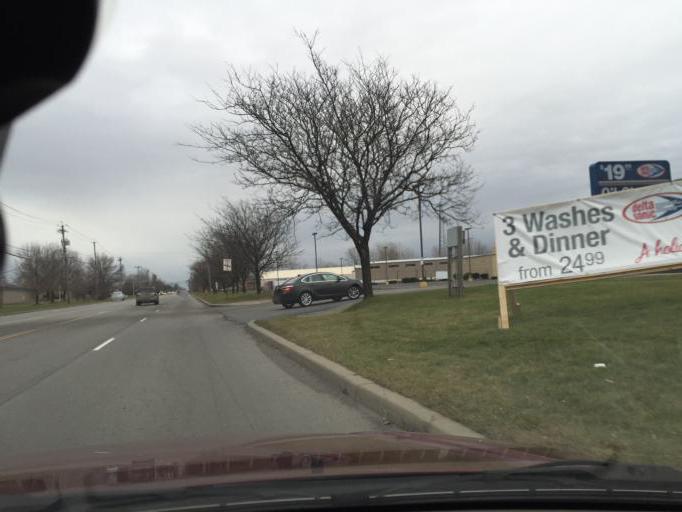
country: US
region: New York
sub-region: Monroe County
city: Rochester
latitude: 43.0940
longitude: -77.6314
